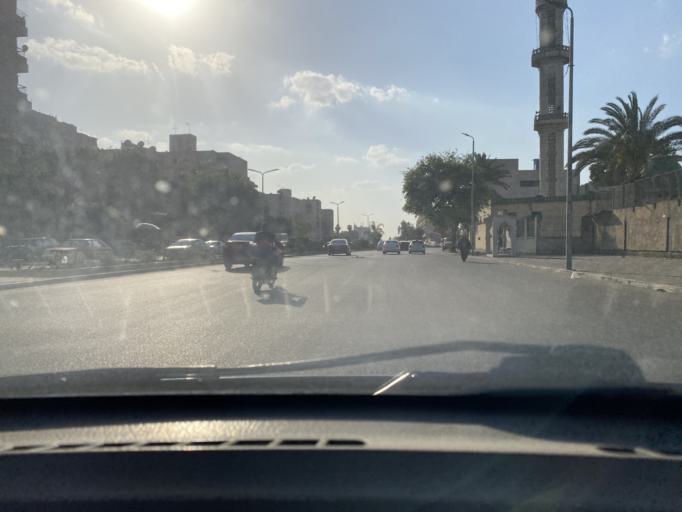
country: EG
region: Muhafazat al Qahirah
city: Cairo
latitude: 30.1032
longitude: 31.3007
